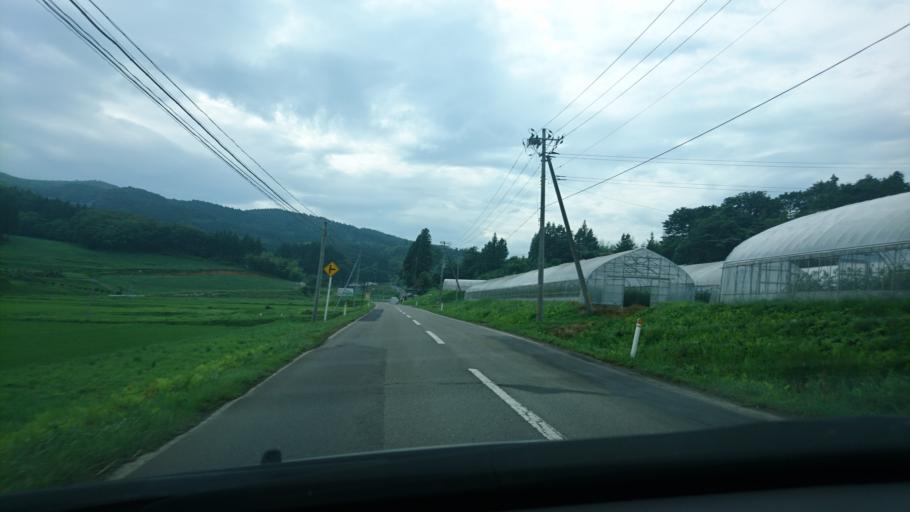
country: JP
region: Iwate
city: Ichinoseki
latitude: 38.9257
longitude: 141.4207
